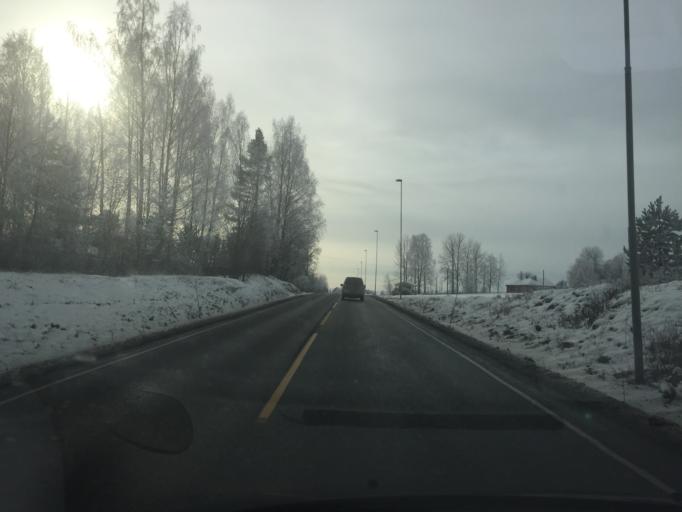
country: NO
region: Hedmark
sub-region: Loten
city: Loten
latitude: 60.8324
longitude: 11.3513
